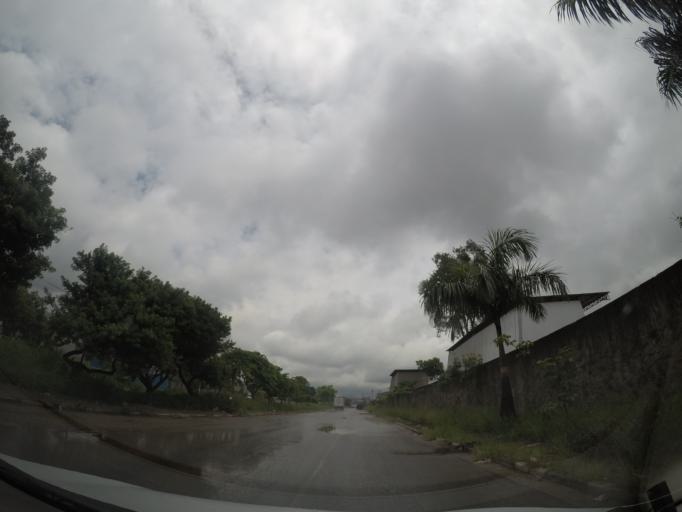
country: BR
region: Sao Paulo
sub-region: Guarulhos
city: Guarulhos
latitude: -23.4662
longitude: -46.4823
